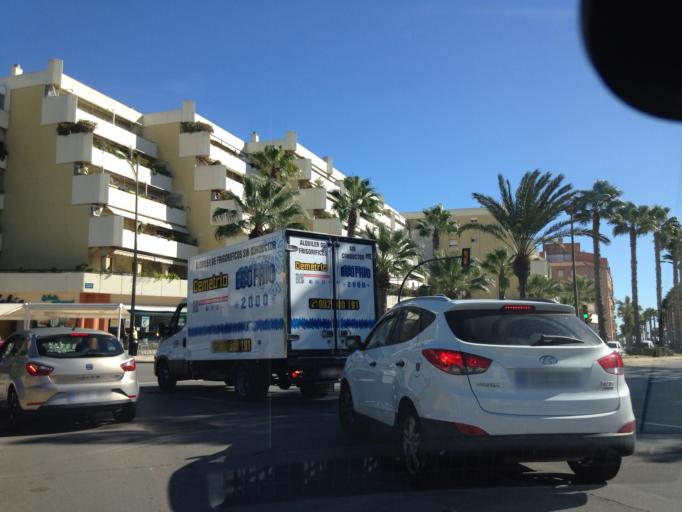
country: ES
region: Andalusia
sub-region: Provincia de Malaga
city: Malaga
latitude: 36.6866
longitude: -4.4528
